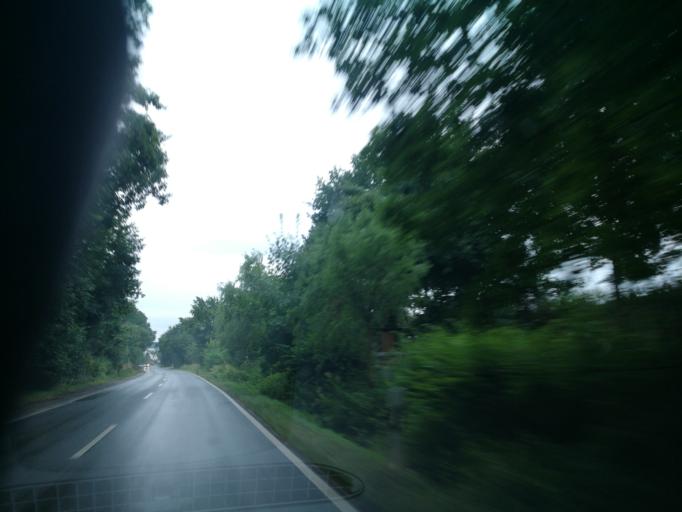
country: DE
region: Bavaria
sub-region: Regierungsbezirk Mittelfranken
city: Veitsbronn
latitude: 49.5151
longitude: 10.8936
